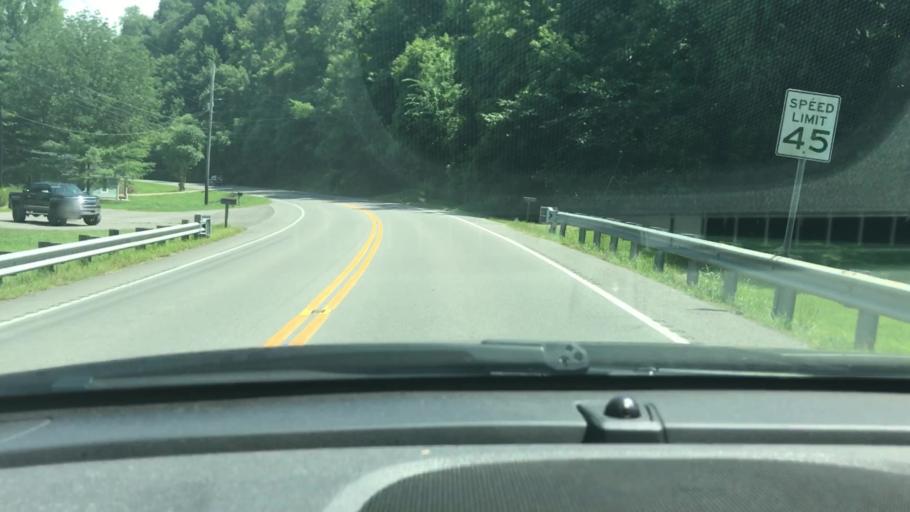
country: US
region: Tennessee
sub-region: Sumner County
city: Shackle Island
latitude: 36.3939
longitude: -86.6285
